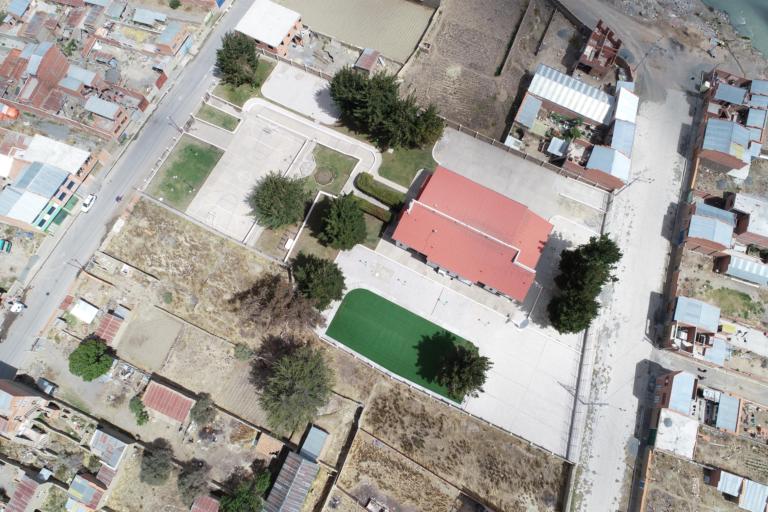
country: BO
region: La Paz
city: Achacachi
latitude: -16.0402
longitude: -68.6841
